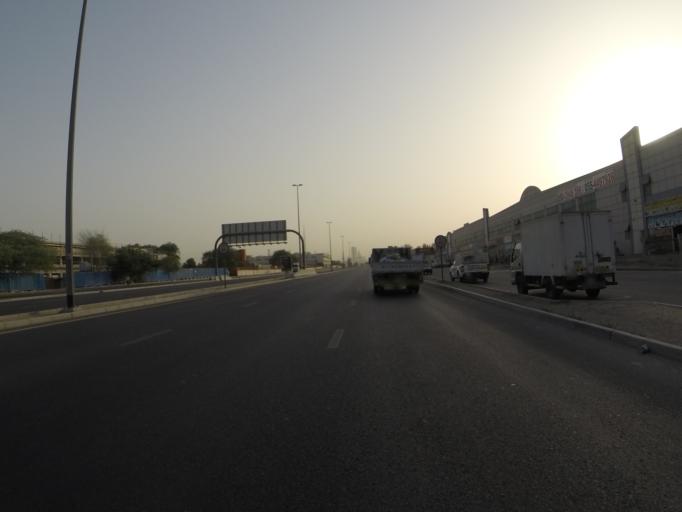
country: AE
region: Dubai
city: Dubai
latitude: 25.1400
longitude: 55.2407
